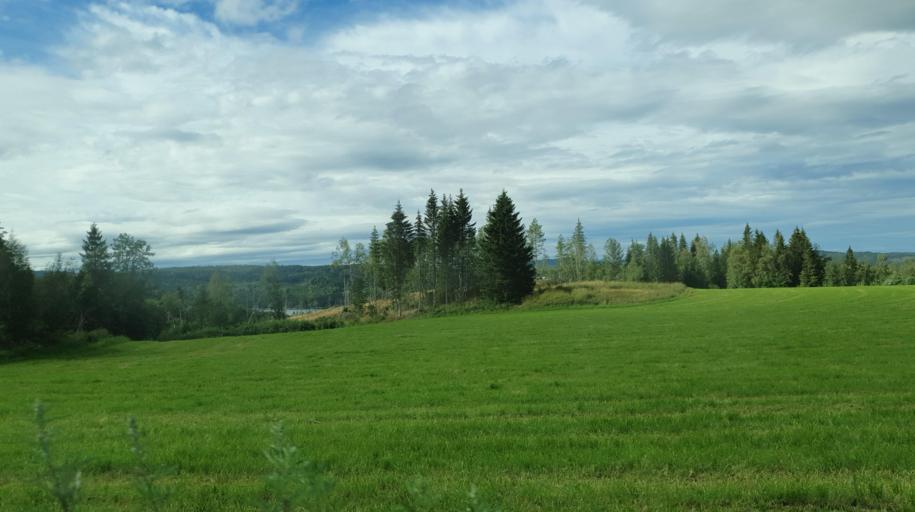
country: NO
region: Nord-Trondelag
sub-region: Levanger
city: Skogn
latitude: 63.6008
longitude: 11.2751
